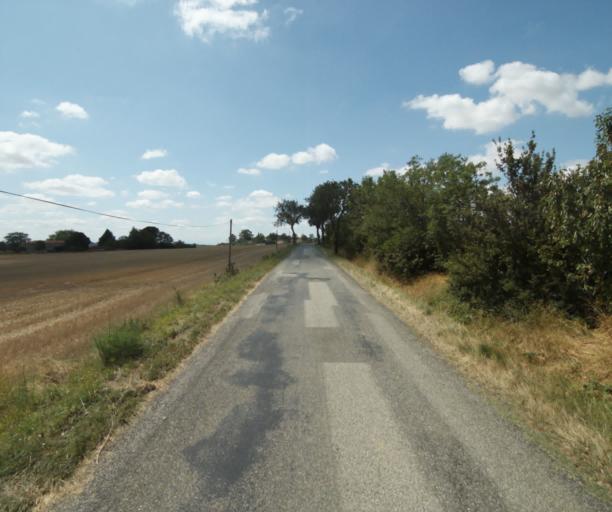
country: FR
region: Midi-Pyrenees
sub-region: Departement de la Haute-Garonne
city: Saint-Felix-Lauragais
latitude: 43.4640
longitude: 1.8414
